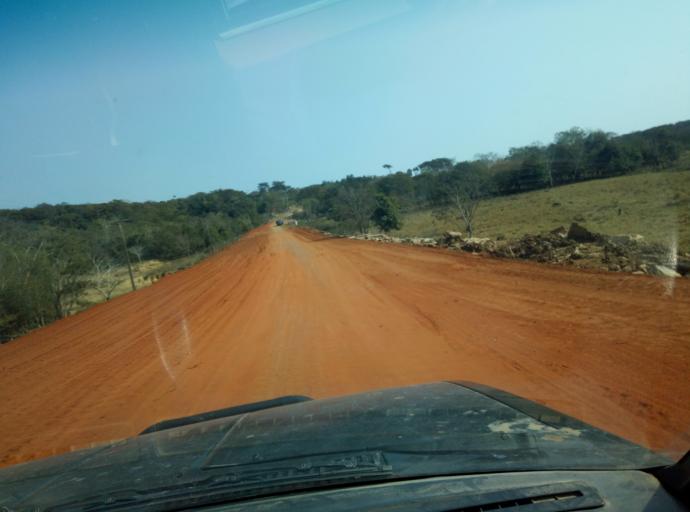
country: PY
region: Caaguazu
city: Coronel Oviedo
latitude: -25.3306
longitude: -56.3191
